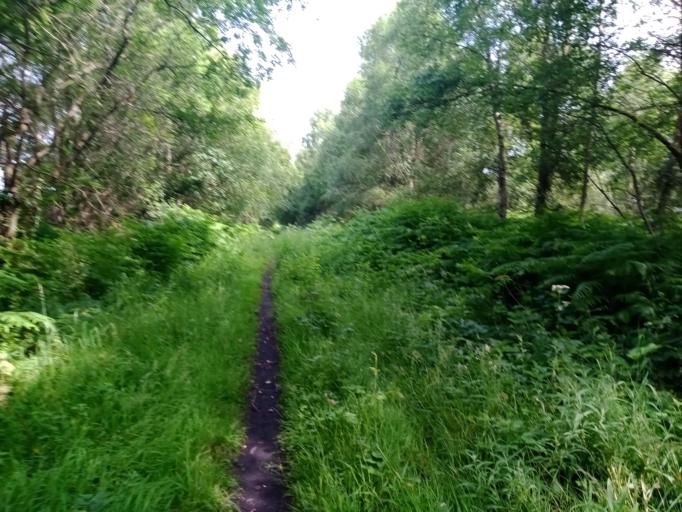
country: IE
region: Leinster
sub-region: Laois
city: Abbeyleix
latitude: 52.8865
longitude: -7.3504
